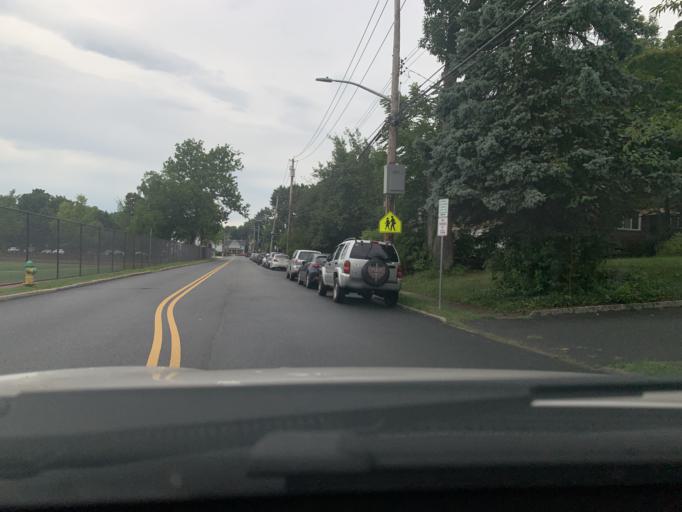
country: US
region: New York
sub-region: Westchester County
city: Ossining
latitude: 41.1589
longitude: -73.8570
